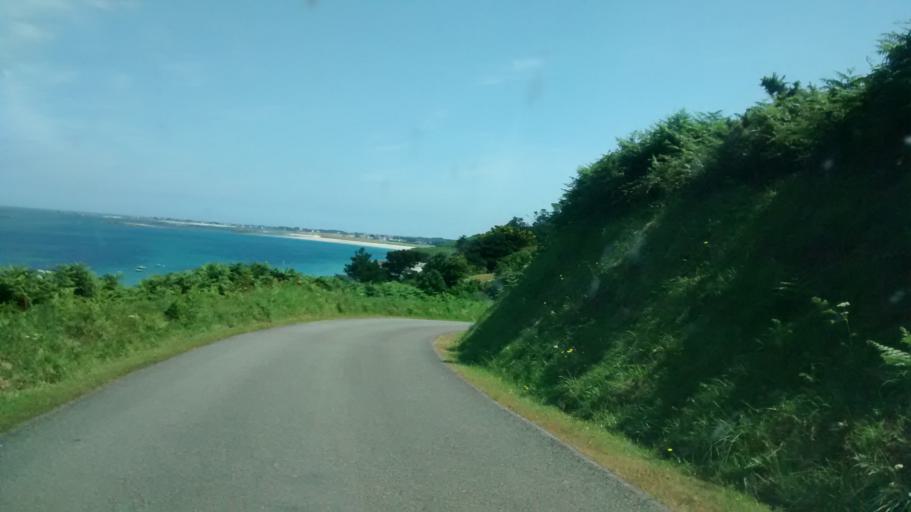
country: FR
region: Brittany
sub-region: Departement du Finistere
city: Plouguerneau
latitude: 48.6224
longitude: -4.4803
